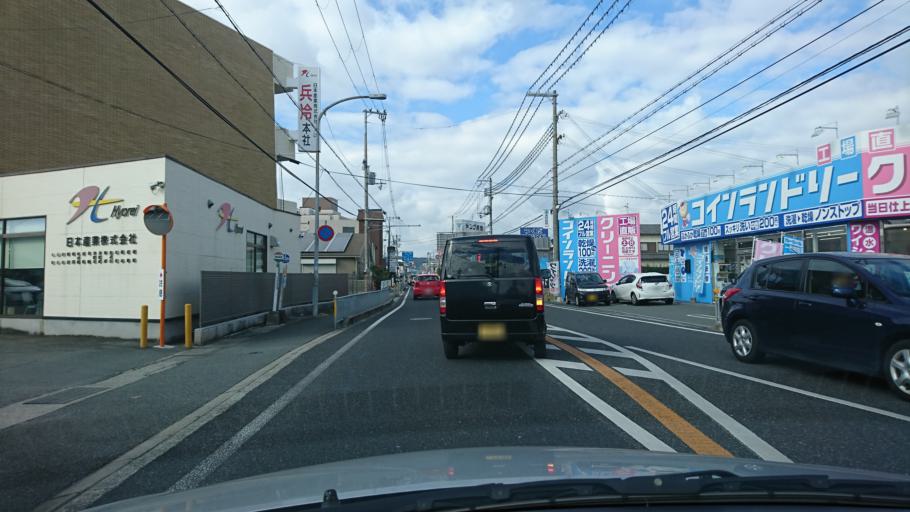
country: JP
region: Hyogo
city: Kakogawacho-honmachi
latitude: 34.7838
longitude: 134.8110
